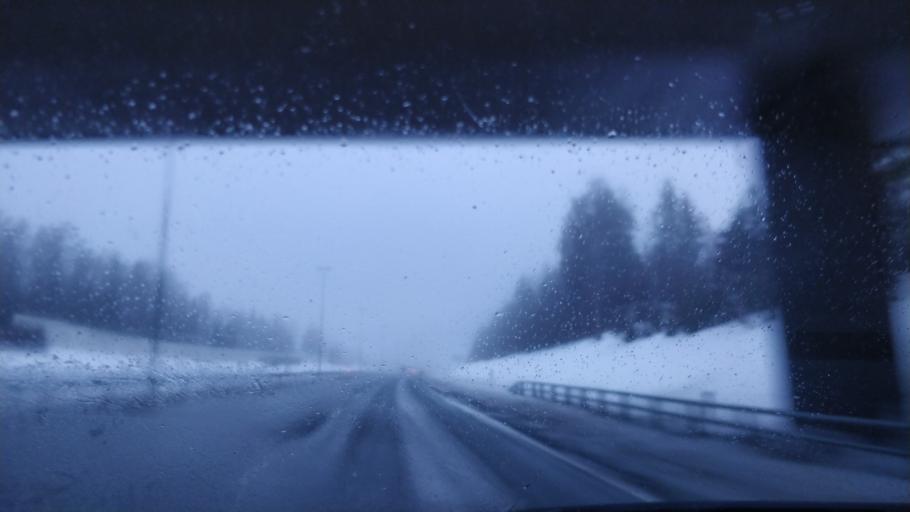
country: FI
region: Lapland
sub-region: Kemi-Tornio
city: Kemi
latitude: 65.7506
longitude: 24.5756
